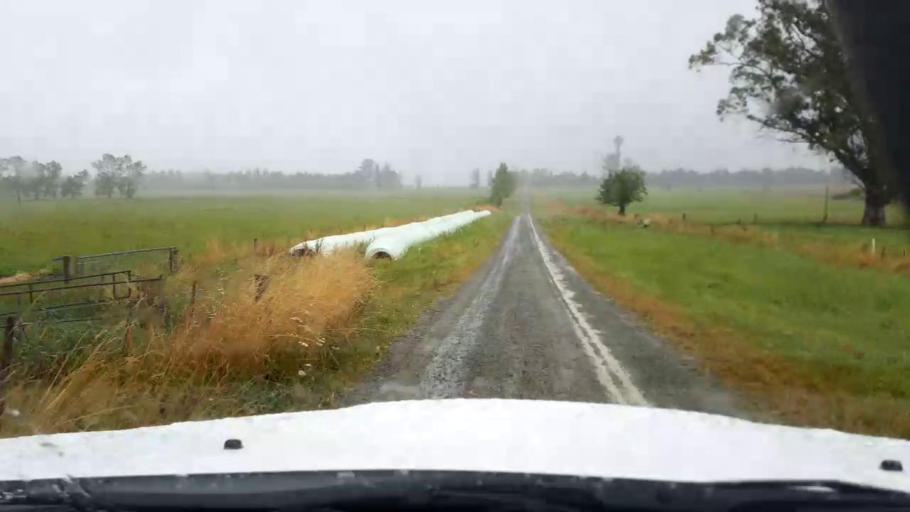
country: NZ
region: Canterbury
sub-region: Timaru District
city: Pleasant Point
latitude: -44.1973
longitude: 171.0910
